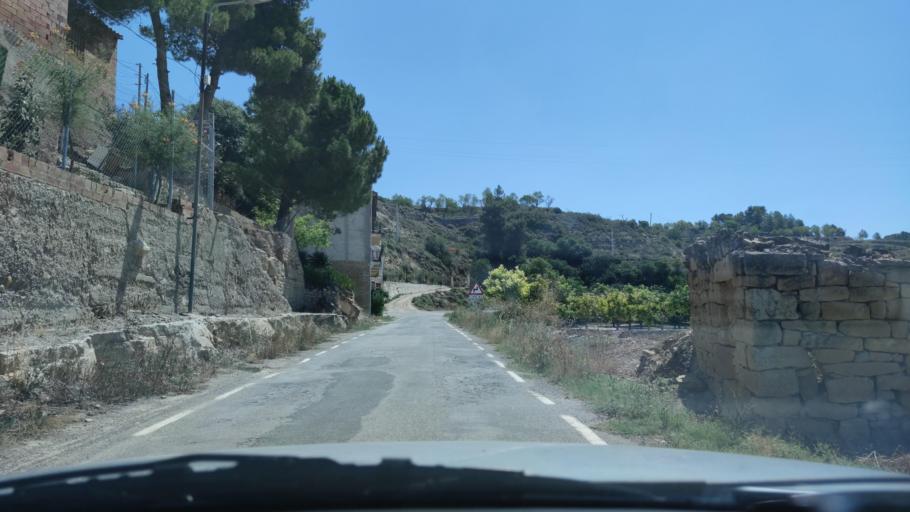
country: ES
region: Catalonia
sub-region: Provincia de Lleida
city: Fulleda
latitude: 41.4932
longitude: 1.0072
